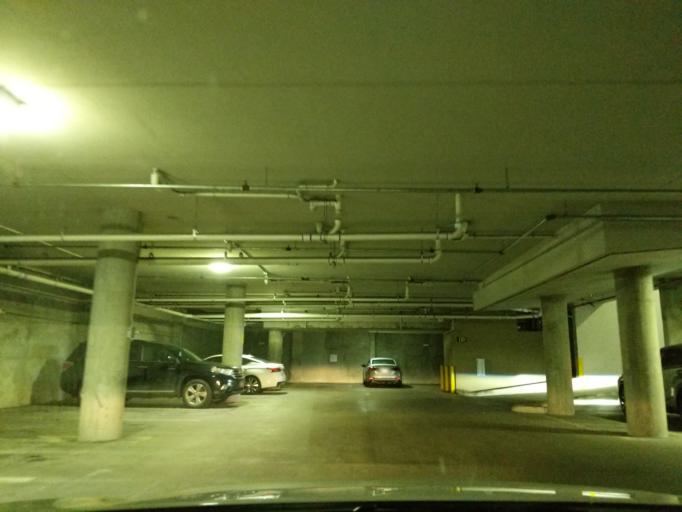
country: US
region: Tennessee
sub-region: Davidson County
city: Belle Meade
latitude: 36.1092
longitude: -86.8195
